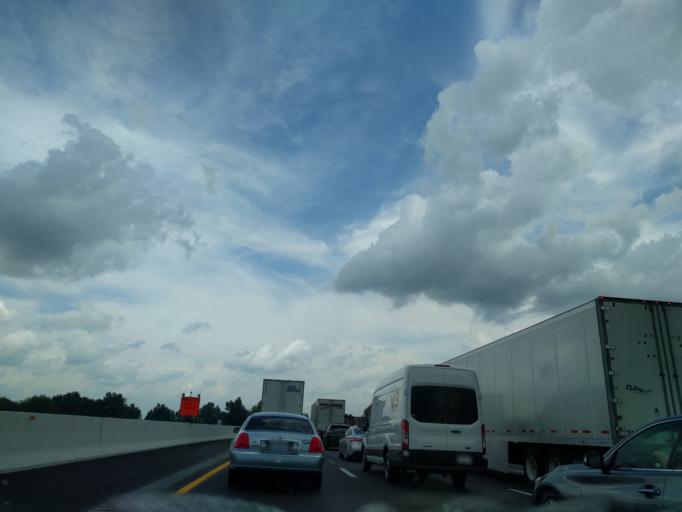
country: US
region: Kentucky
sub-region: Larue County
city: Hodgenville
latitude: 37.5059
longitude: -85.8880
